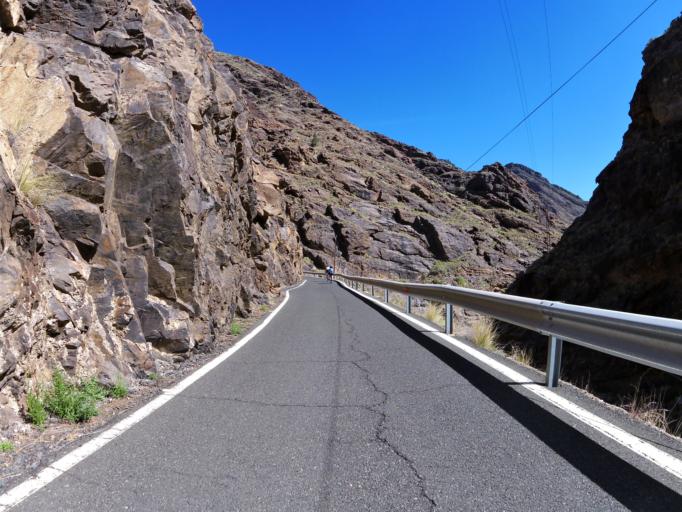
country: ES
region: Canary Islands
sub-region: Provincia de Las Palmas
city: San Nicolas
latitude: 27.9890
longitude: -15.7160
